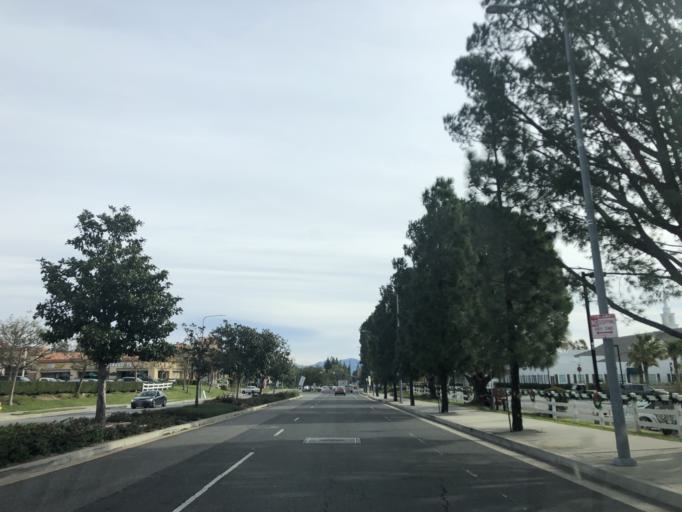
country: US
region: California
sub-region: Los Angeles County
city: Chatsworth
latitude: 34.2748
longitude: -118.5648
